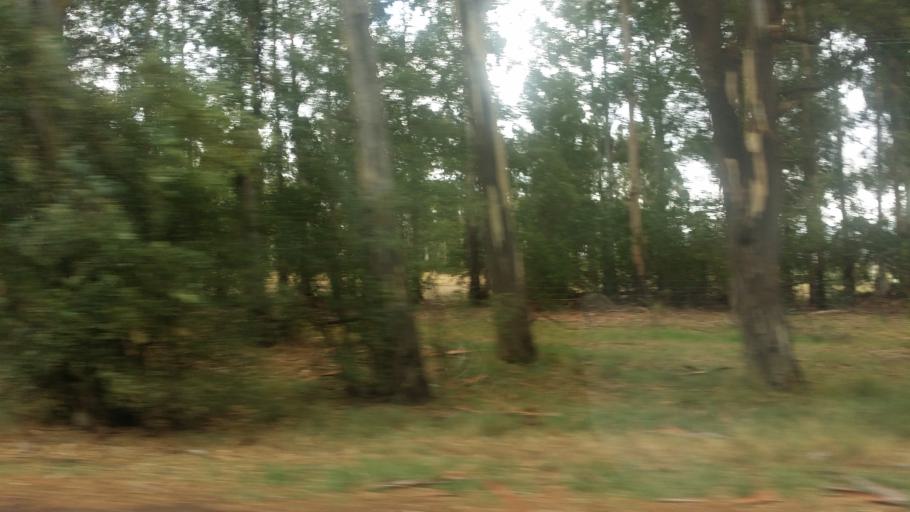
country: AR
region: La Pampa
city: Santa Rosa
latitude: -36.6031
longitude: -64.2306
